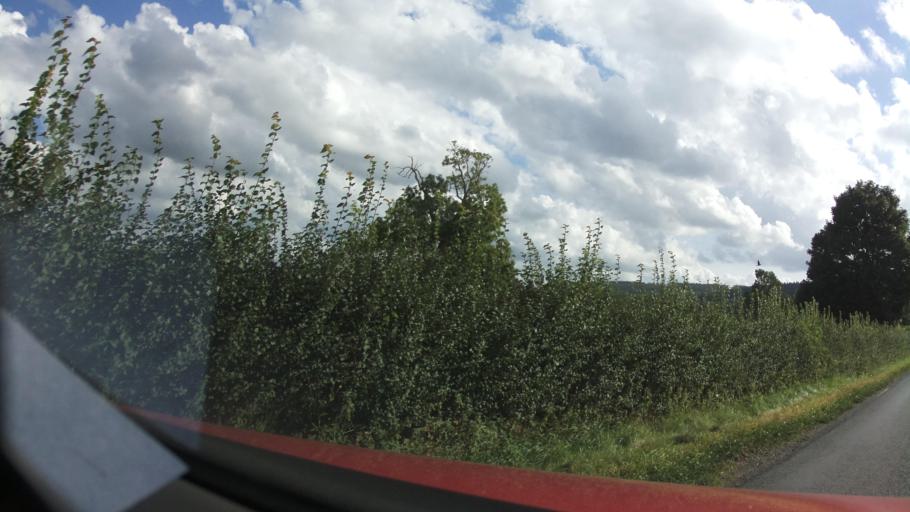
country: GB
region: England
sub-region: North Yorkshire
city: Leyburn
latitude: 54.2747
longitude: -1.7792
